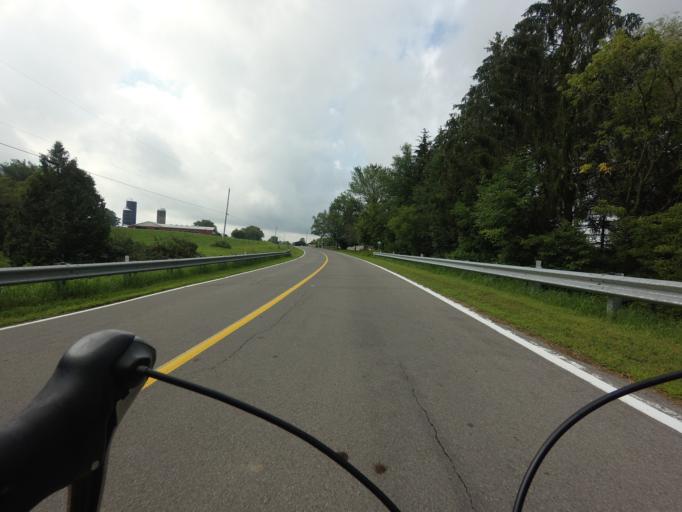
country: CA
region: Ontario
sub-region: Lanark County
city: Smiths Falls
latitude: 44.9718
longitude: -75.8086
